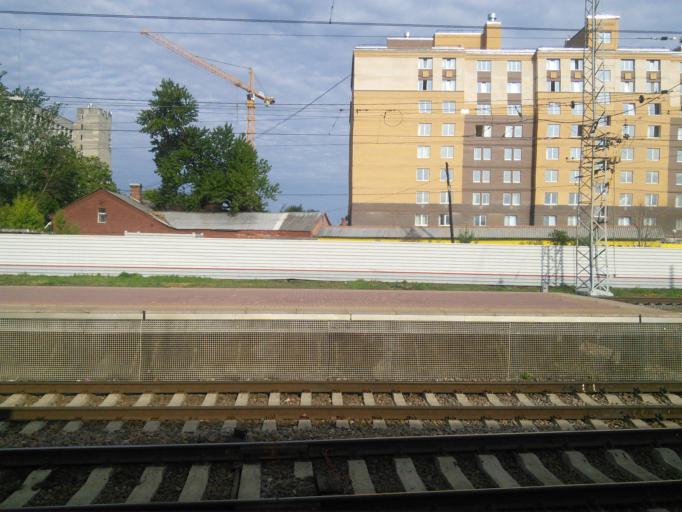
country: RU
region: Leningrad
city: Finlyandskiy
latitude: 59.9597
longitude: 30.3584
